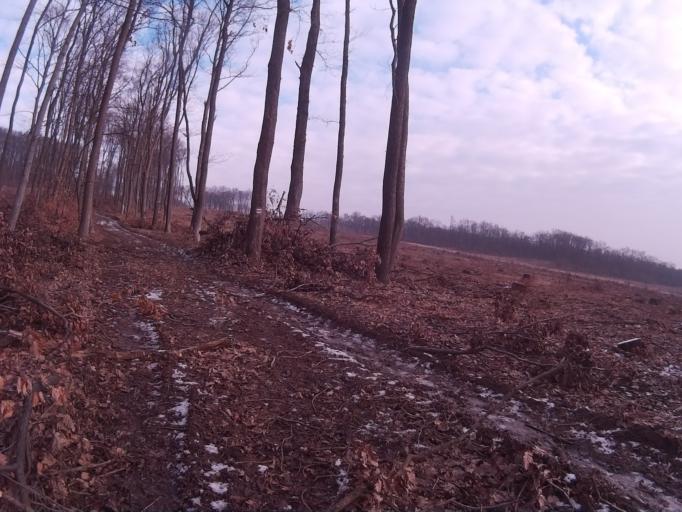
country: HU
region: Komarom-Esztergom
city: Tarjan
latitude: 47.6697
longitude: 18.5040
